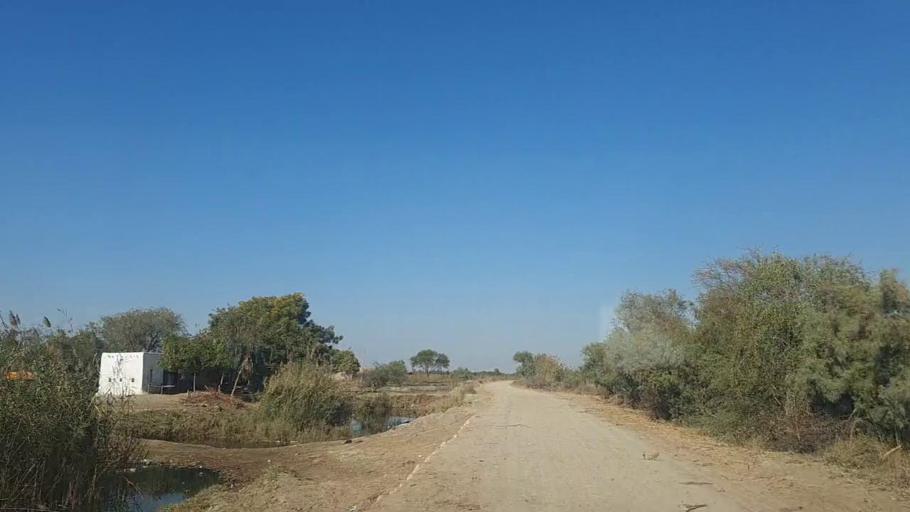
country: PK
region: Sindh
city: Sanghar
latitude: 26.2210
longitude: 68.9646
